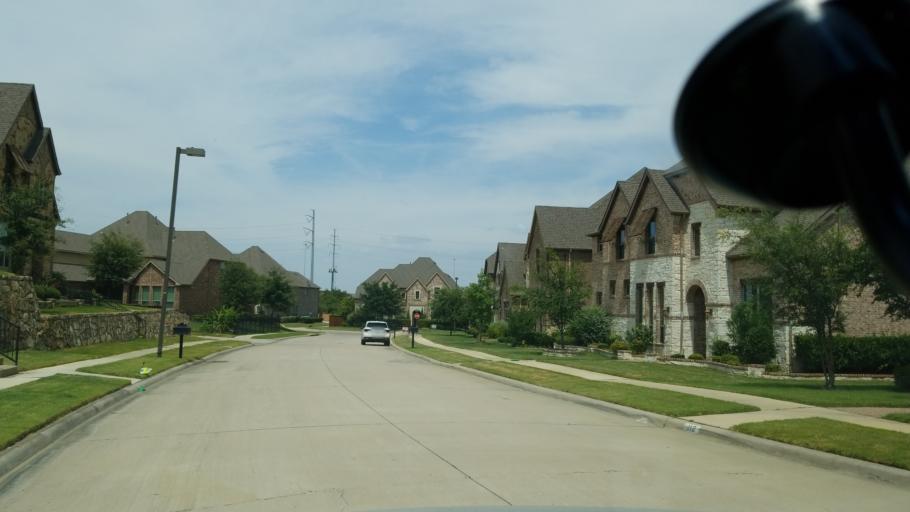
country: US
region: Texas
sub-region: Dallas County
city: Farmers Branch
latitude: 32.9064
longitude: -96.9459
